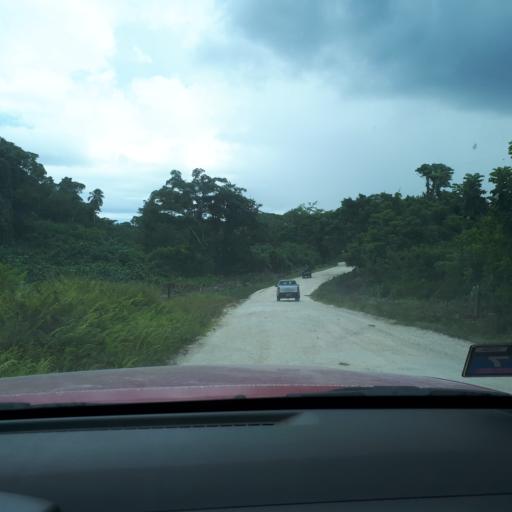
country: VU
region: Sanma
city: Luganville
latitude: -15.5783
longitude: 167.0299
